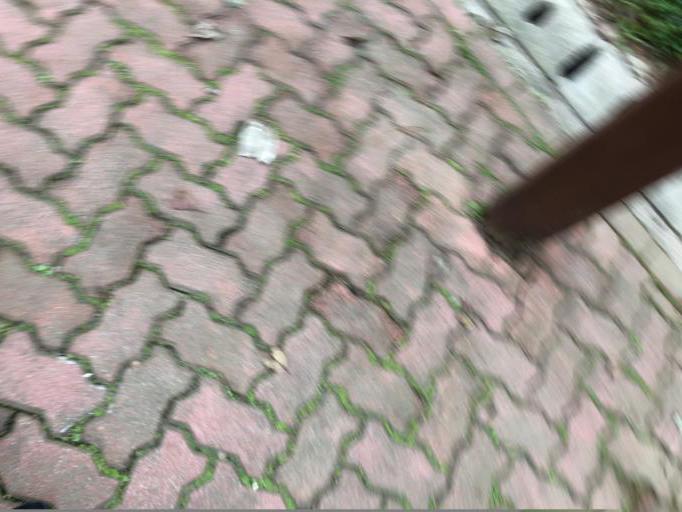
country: HK
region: Tai Po
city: Tai Po
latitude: 22.4693
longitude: 114.1941
